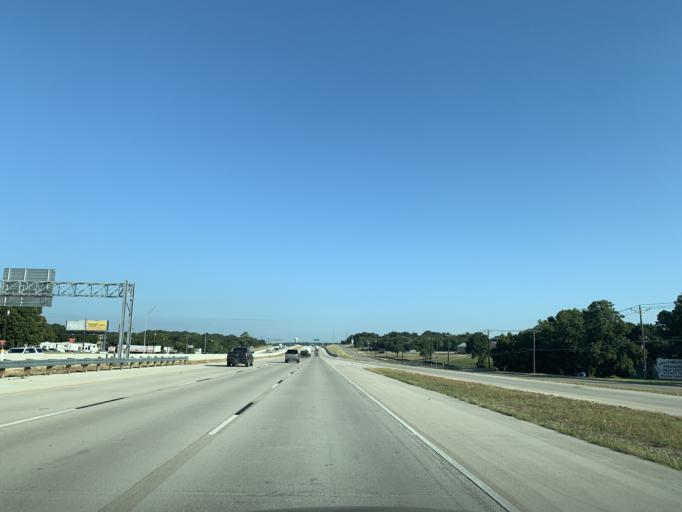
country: US
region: Texas
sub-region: Tarrant County
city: Lakeside
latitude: 32.8418
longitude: -97.4955
